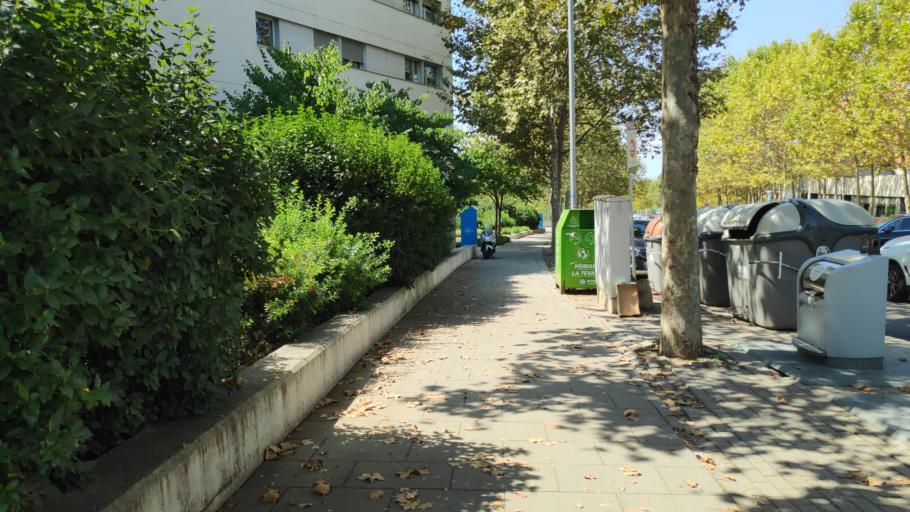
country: ES
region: Catalonia
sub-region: Provincia de Barcelona
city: Sant Cugat del Valles
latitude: 41.4701
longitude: 2.0604
